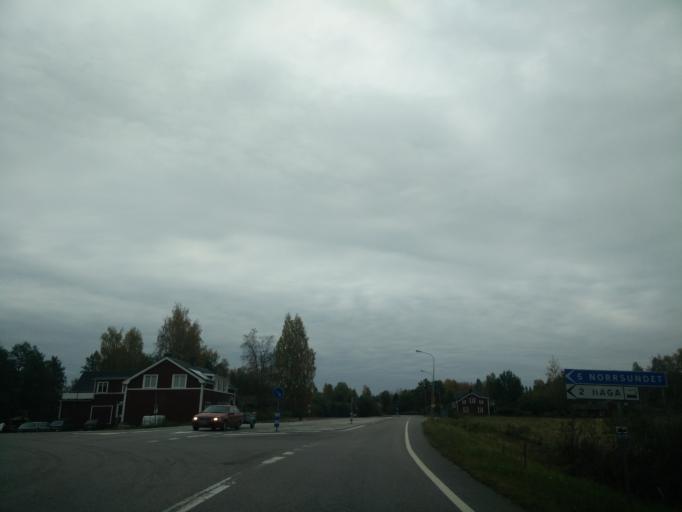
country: SE
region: Gaevleborg
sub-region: Gavle Kommun
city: Norrsundet
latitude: 60.8985
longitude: 17.0674
